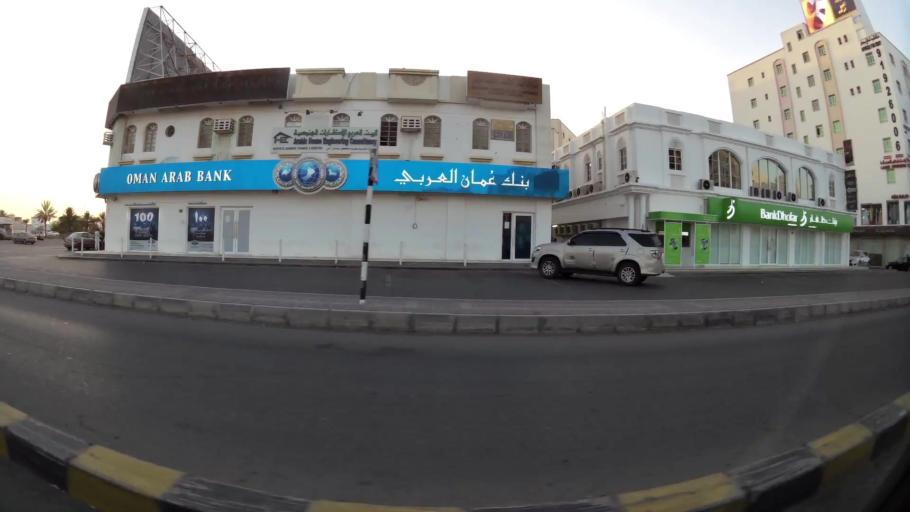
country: OM
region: Muhafazat Masqat
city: As Sib al Jadidah
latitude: 23.6400
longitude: 58.2040
